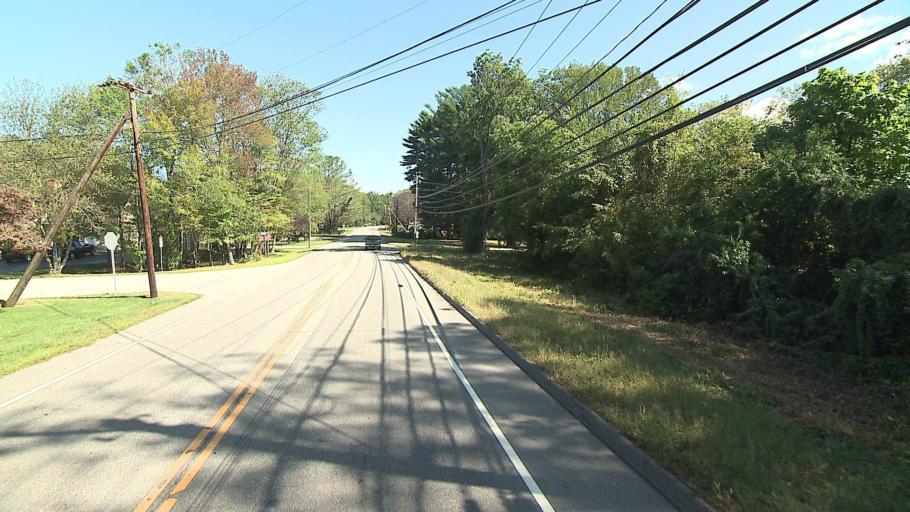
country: US
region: Connecticut
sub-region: Windham County
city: East Brooklyn
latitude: 41.7764
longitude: -71.8950
